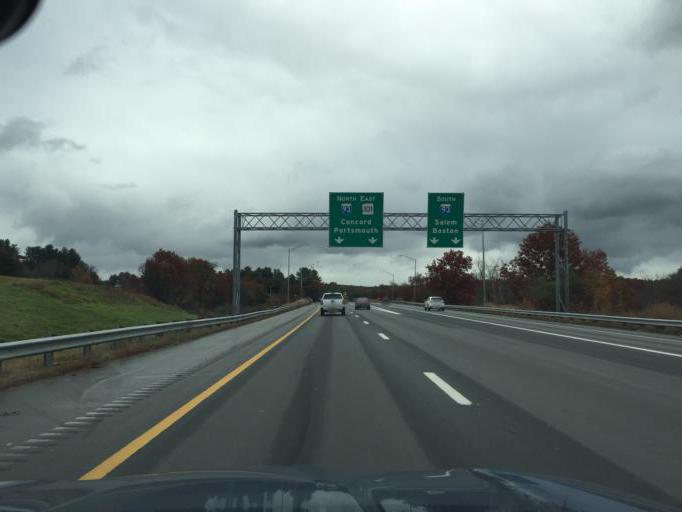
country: US
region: New Hampshire
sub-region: Hillsborough County
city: Manchester
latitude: 42.9606
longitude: -71.4201
